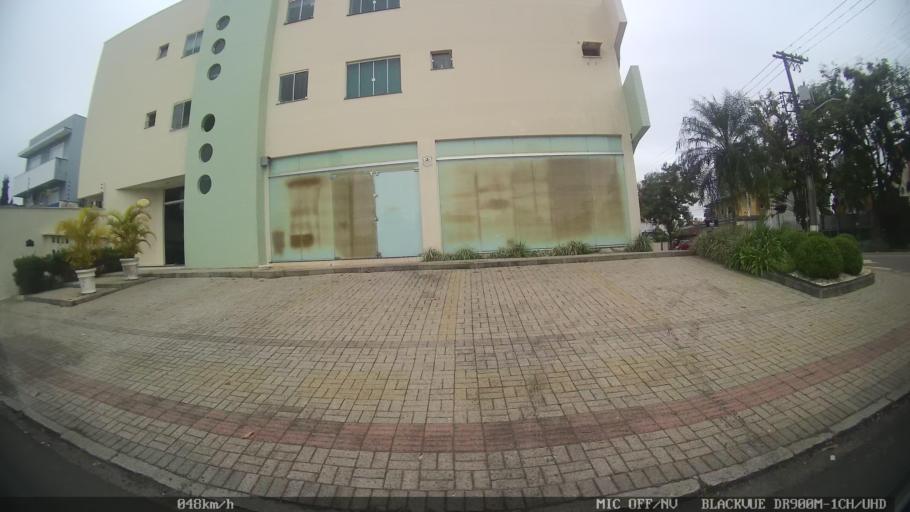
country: BR
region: Santa Catarina
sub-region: Joinville
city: Joinville
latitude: -26.2753
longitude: -48.8477
